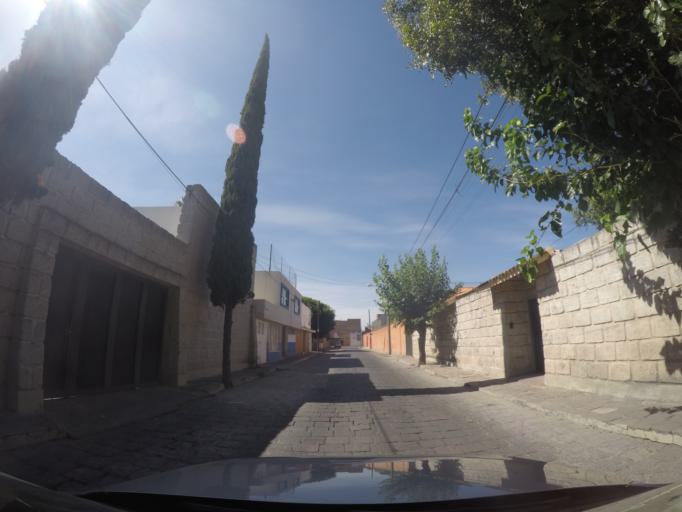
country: MX
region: San Luis Potosi
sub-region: San Luis Potosi
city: San Luis Potosi
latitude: 22.1496
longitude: -101.0126
